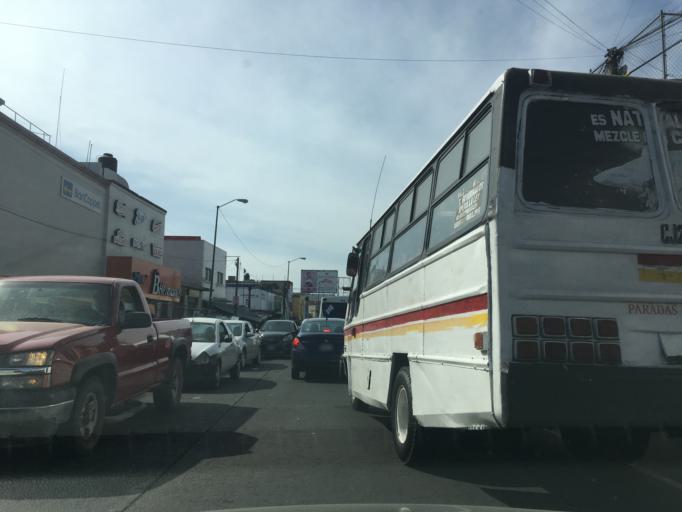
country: MX
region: Michoacan
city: Morelia
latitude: 19.6959
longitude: -101.1911
